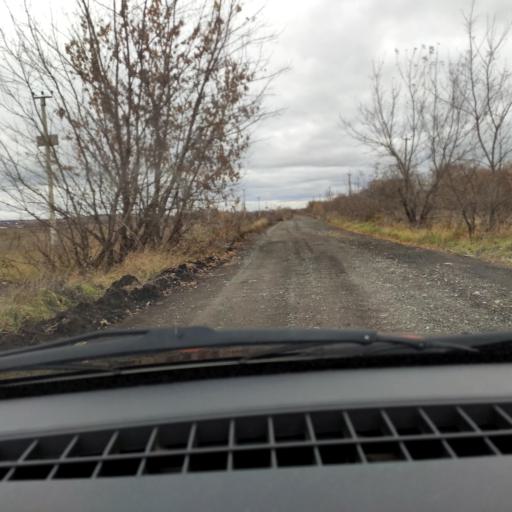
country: RU
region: Bashkortostan
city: Avdon
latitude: 54.4968
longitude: 55.8656
